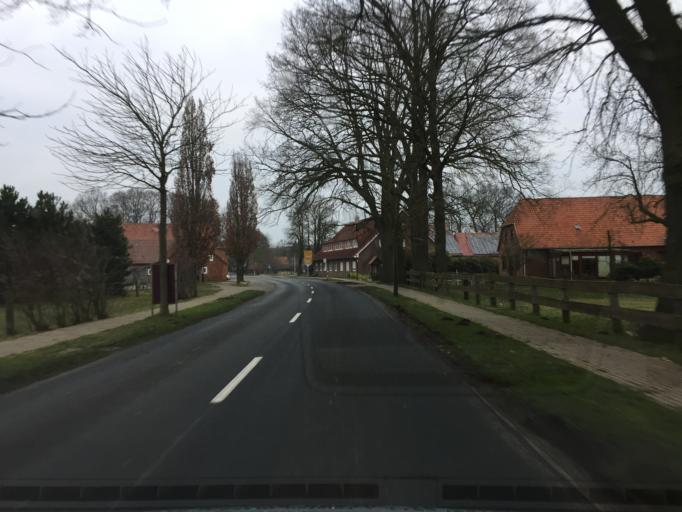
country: DE
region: Lower Saxony
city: Schwaforden
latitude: 52.7365
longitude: 8.8185
